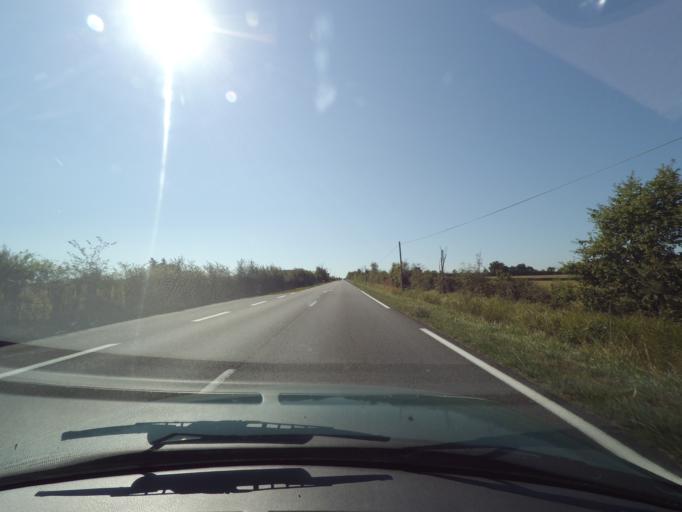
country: FR
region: Poitou-Charentes
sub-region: Departement de la Vienne
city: Lussac-les-Chateaux
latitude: 46.3716
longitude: 0.7623
